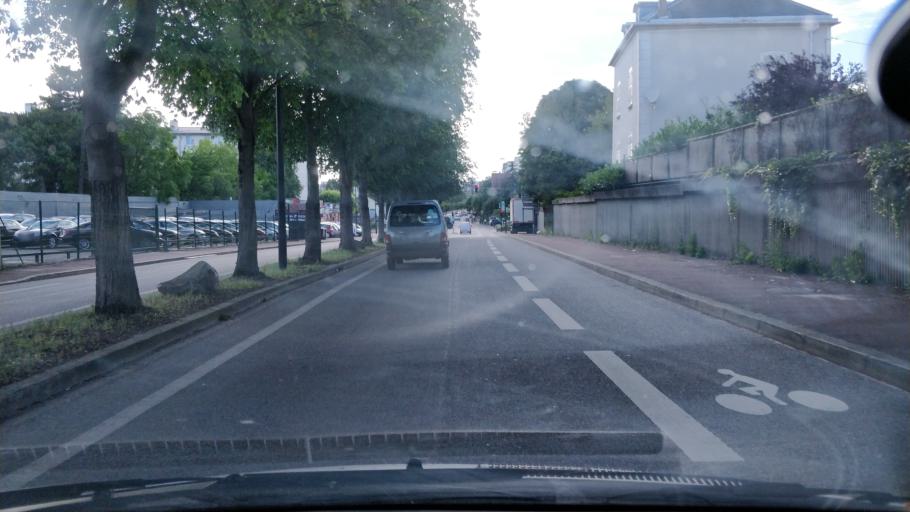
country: FR
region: Ile-de-France
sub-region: Departement de Seine-Saint-Denis
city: Gagny
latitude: 48.8823
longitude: 2.5368
